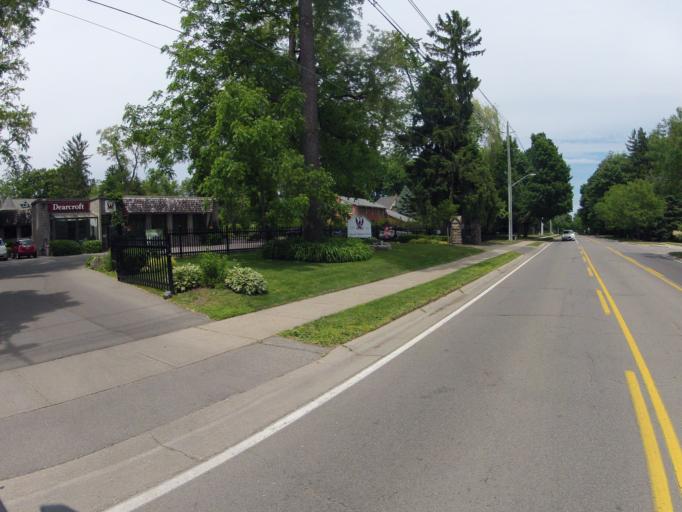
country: CA
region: Ontario
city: Oakville
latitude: 43.4587
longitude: -79.6543
